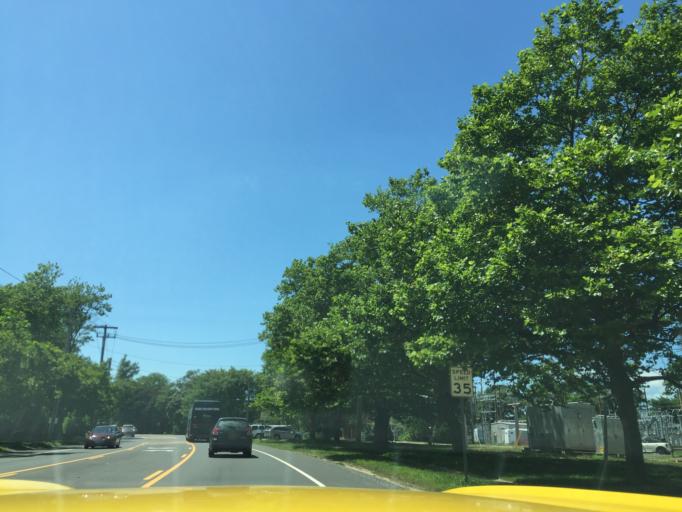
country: US
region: New York
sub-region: Suffolk County
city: Amagansett
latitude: 40.9796
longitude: -72.1304
